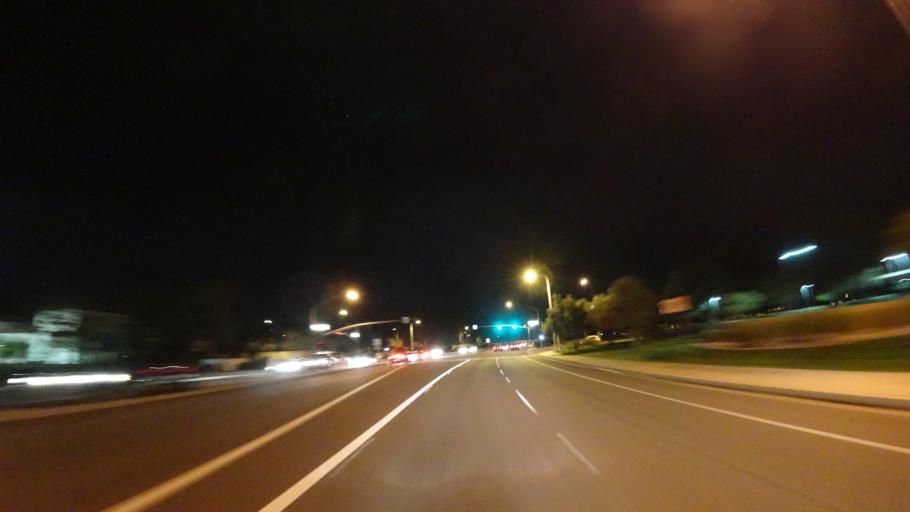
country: US
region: Arizona
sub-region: Maricopa County
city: Chandler
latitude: 33.2592
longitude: -111.8585
